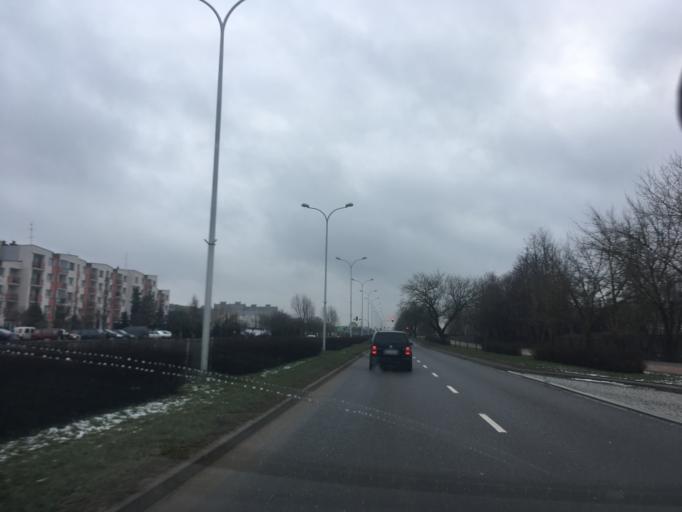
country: PL
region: Podlasie
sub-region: Suwalki
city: Suwalki
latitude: 54.1232
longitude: 22.9295
